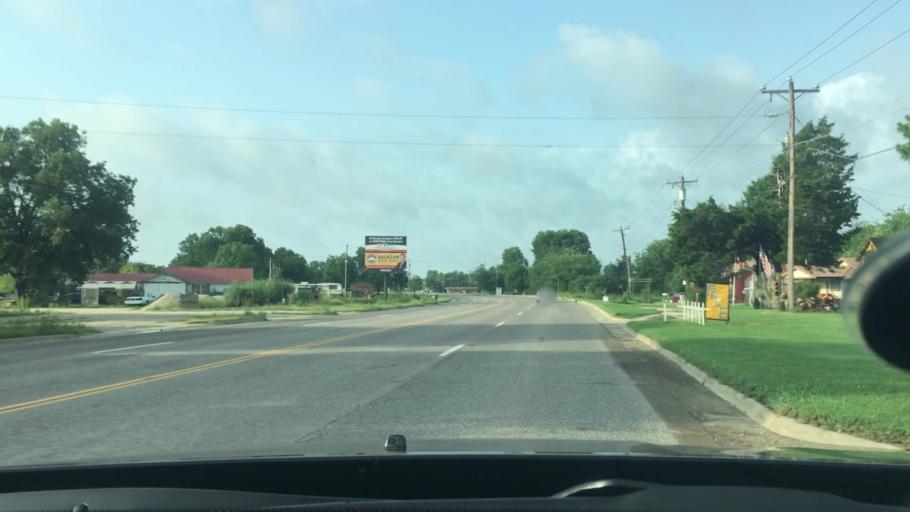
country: US
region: Oklahoma
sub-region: Murray County
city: Davis
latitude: 34.4878
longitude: -97.1298
